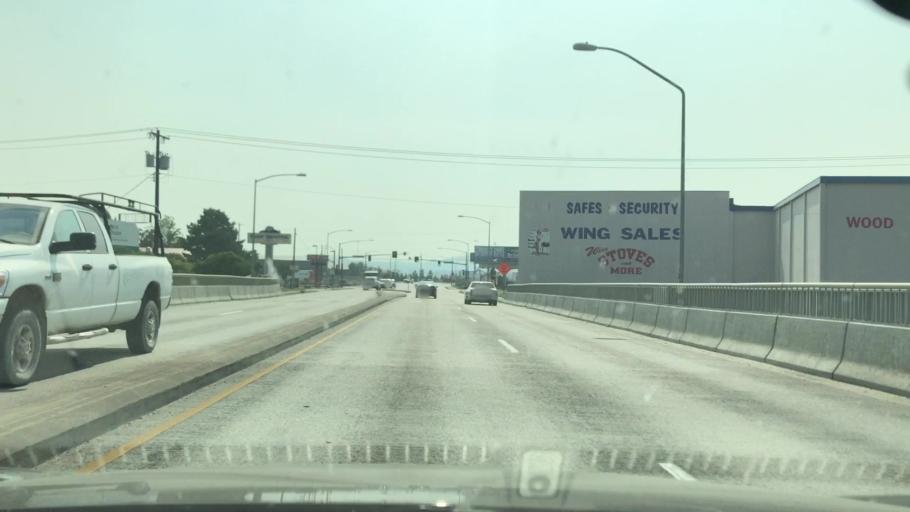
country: US
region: Washington
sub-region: Spokane County
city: Spokane
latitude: 47.6695
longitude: -117.3615
